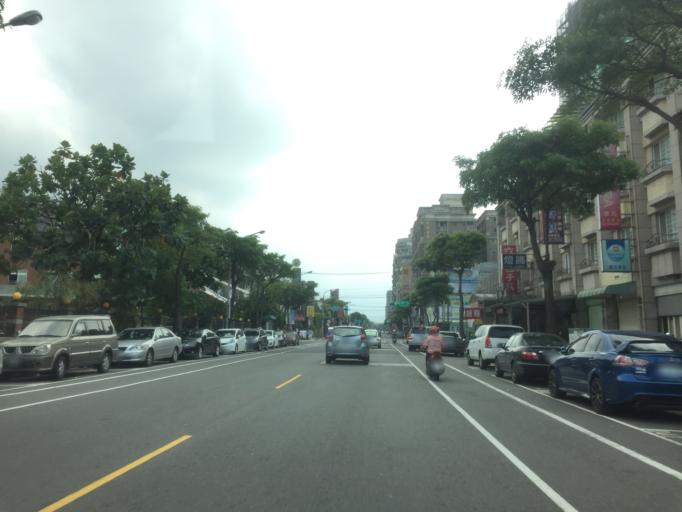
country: TW
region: Taiwan
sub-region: Taoyuan
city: Taoyuan
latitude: 24.9655
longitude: 121.3068
